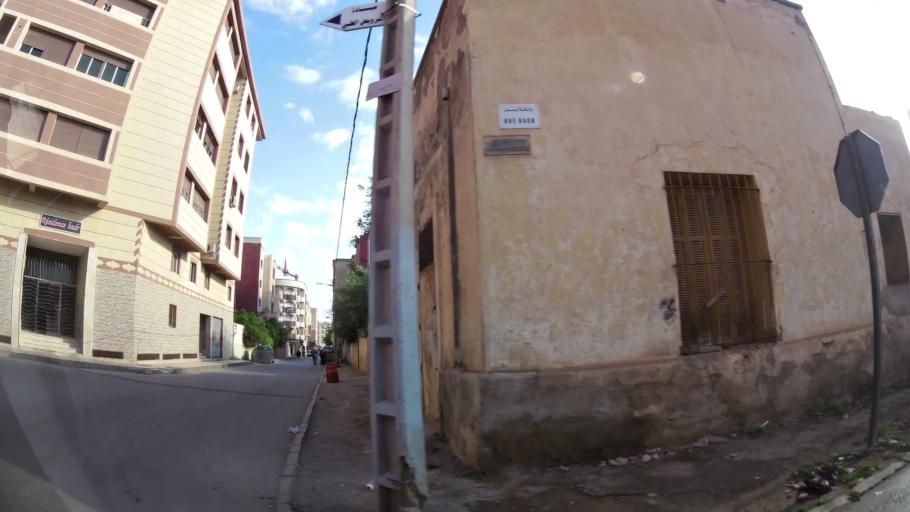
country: MA
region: Oriental
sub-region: Oujda-Angad
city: Oujda
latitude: 34.6740
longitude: -1.9224
